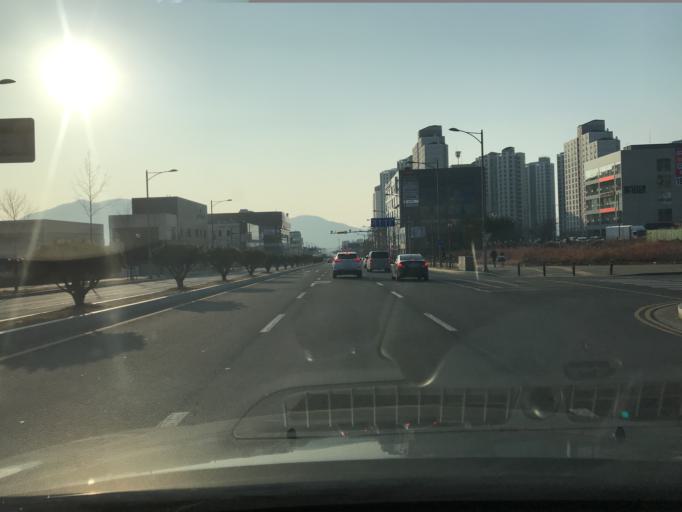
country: KR
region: Daegu
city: Hwawon
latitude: 35.6891
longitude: 128.4558
